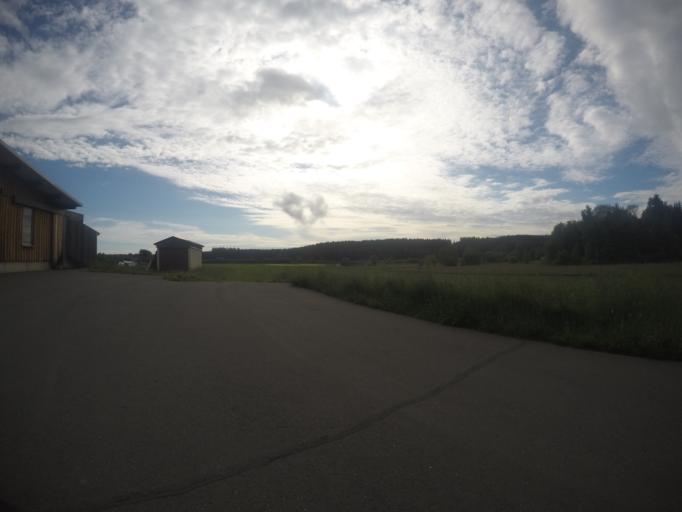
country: DE
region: Bavaria
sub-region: Upper Franconia
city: Schonwald
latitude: 50.1993
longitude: 12.0975
